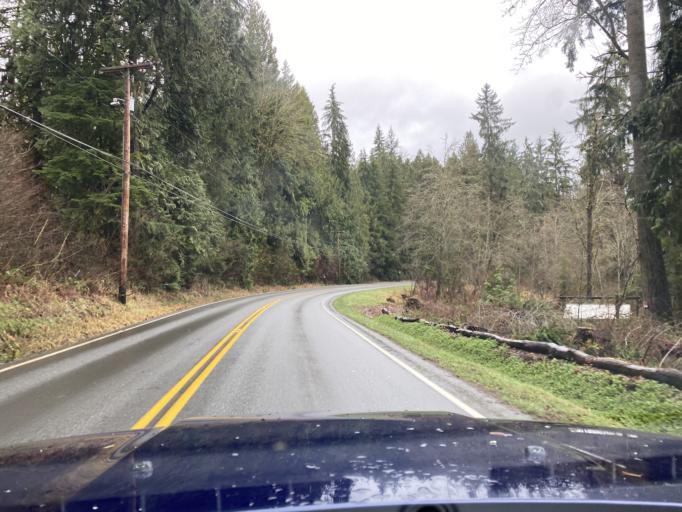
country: US
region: Washington
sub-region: King County
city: Duvall
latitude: 47.7365
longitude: -122.0149
